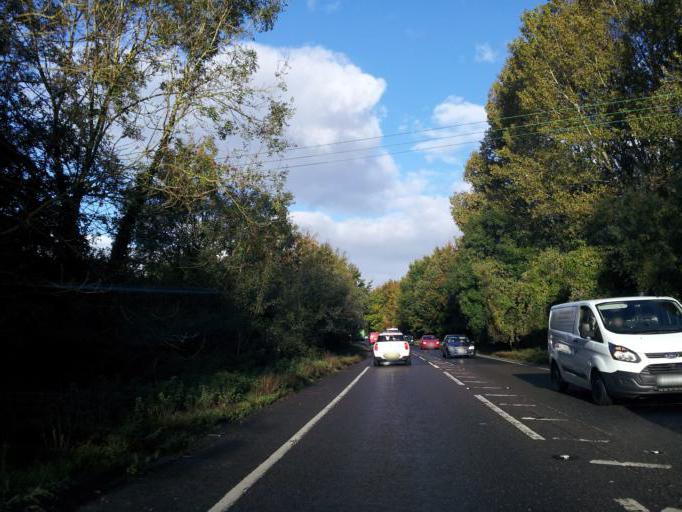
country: GB
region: England
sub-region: Norfolk
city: Mattishall
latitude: 52.6634
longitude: 1.1127
